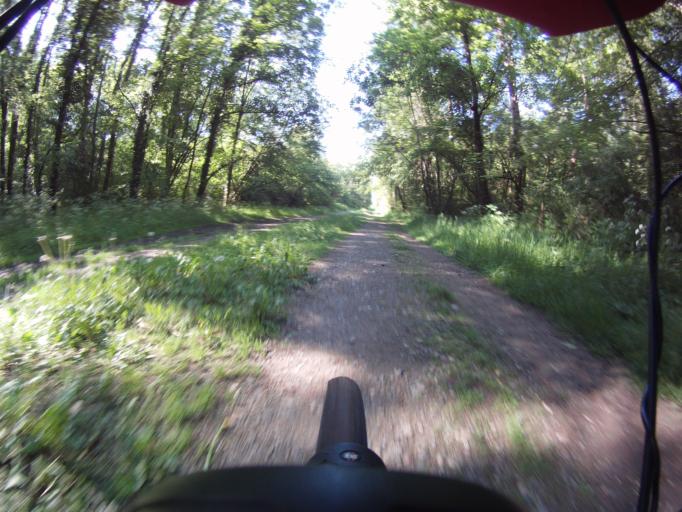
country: FR
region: Auvergne
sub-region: Departement du Puy-de-Dome
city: Dallet
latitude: 45.7674
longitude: 3.2356
